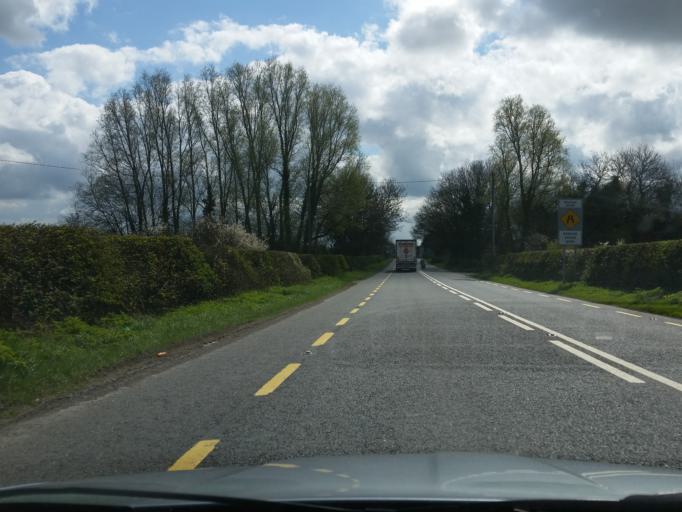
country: IE
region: Leinster
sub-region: An Mhi
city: Ratoath
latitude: 53.5635
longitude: -6.4437
